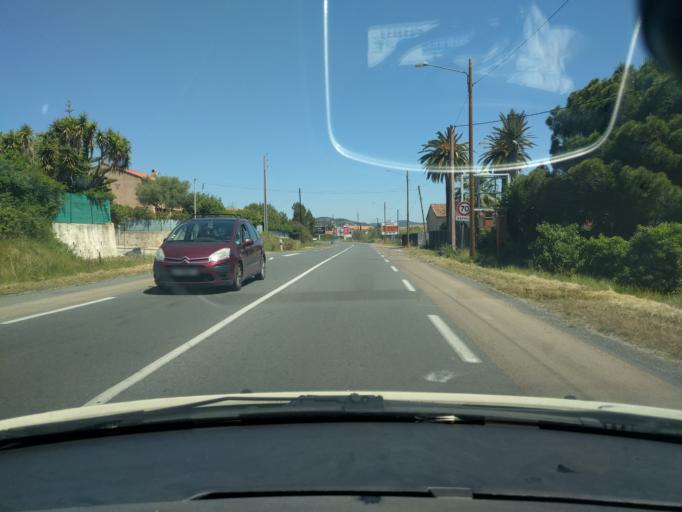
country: FR
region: Provence-Alpes-Cote d'Azur
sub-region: Departement du Var
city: Hyeres
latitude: 43.0947
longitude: 6.1311
